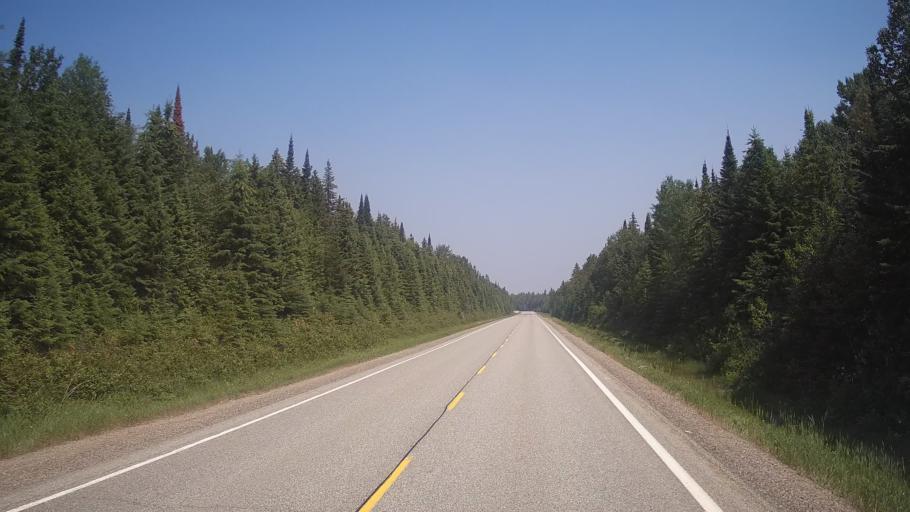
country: CA
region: Ontario
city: Timmins
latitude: 48.2103
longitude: -81.5747
